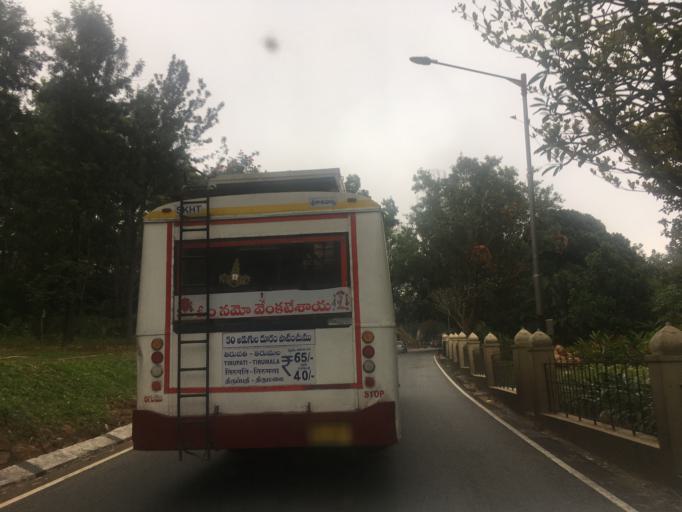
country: IN
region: Andhra Pradesh
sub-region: Chittoor
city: Tirumala
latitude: 13.6693
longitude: 79.3506
